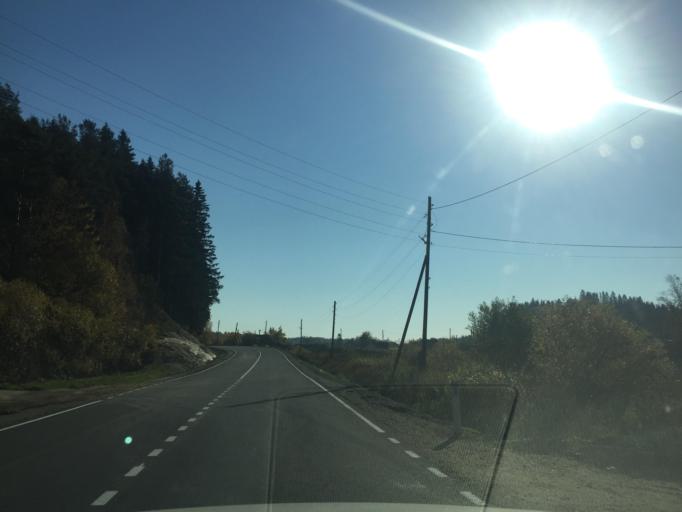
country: RU
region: Leningrad
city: Kuznechnoye
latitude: 61.3040
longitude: 29.8815
